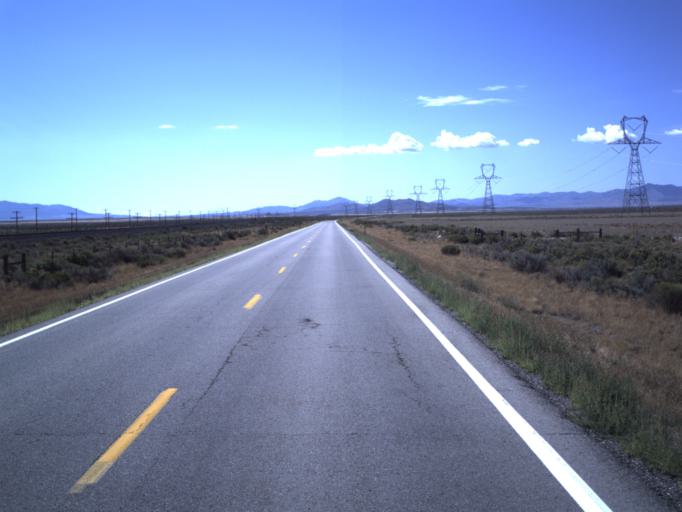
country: US
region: Utah
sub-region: Tooele County
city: Tooele
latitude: 40.2833
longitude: -112.3992
